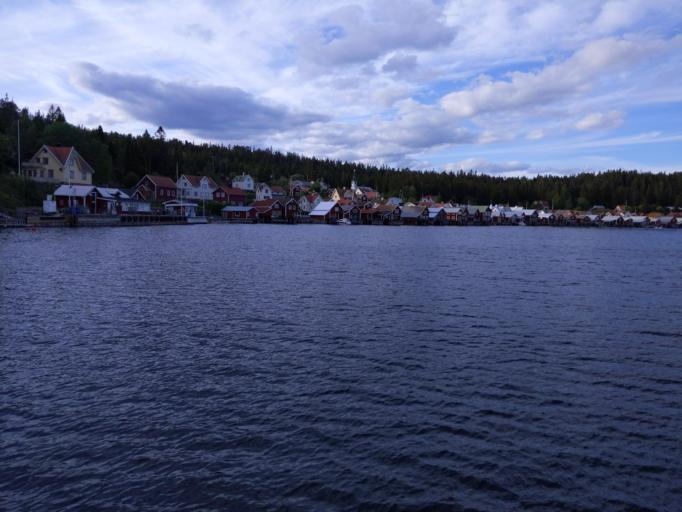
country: SE
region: Vaesternorrland
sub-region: OErnskoeldsviks Kommun
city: Kopmanholmen
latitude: 63.0192
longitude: 18.6471
